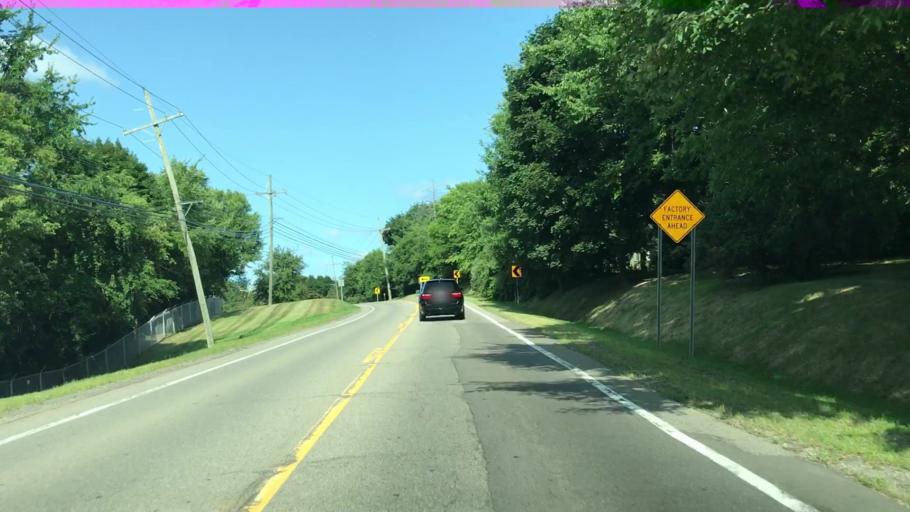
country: US
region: Michigan
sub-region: Oakland County
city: Rochester
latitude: 42.6879
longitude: -83.1161
